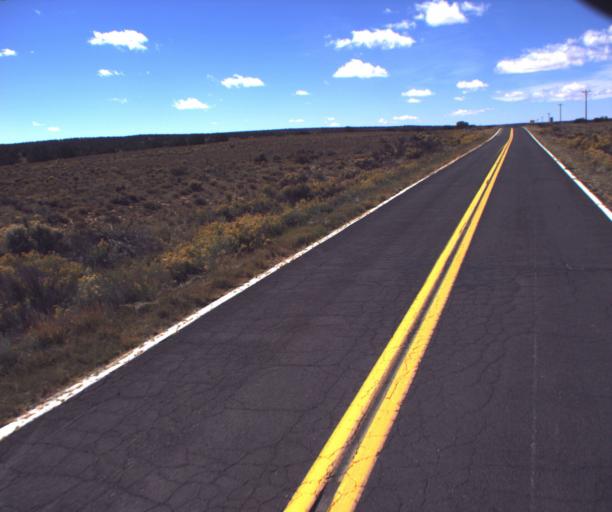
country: US
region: New Mexico
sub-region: McKinley County
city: Zuni Pueblo
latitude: 35.0191
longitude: -109.0488
